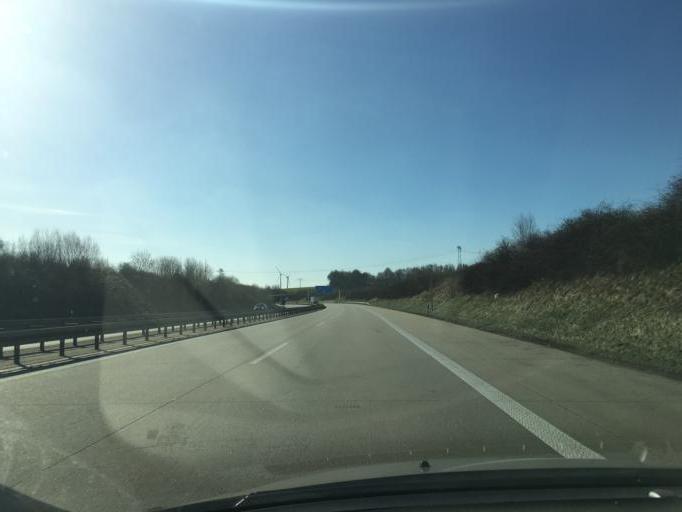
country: DE
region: Saxony
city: Hartmannsdorf
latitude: 50.8619
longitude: 12.8171
